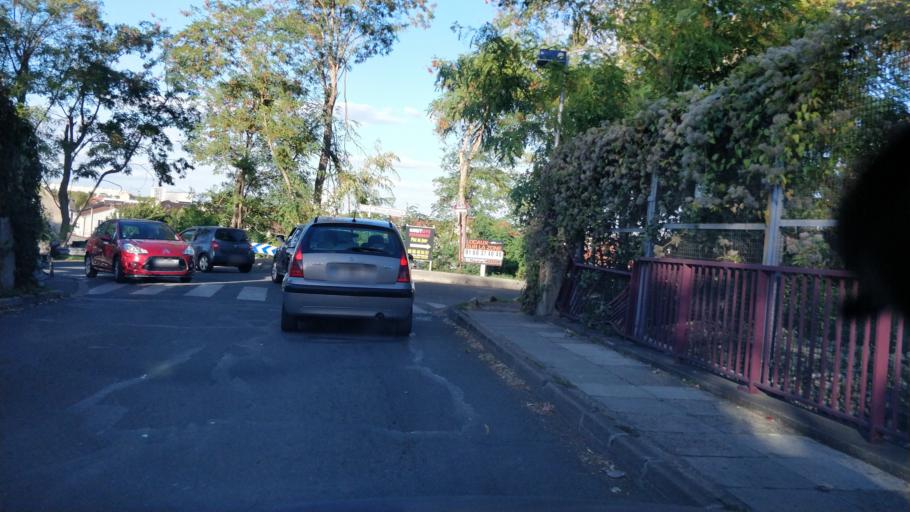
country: FR
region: Ile-de-France
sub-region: Departement de Seine-Saint-Denis
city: Noisy-le-Sec
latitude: 48.8890
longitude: 2.4777
